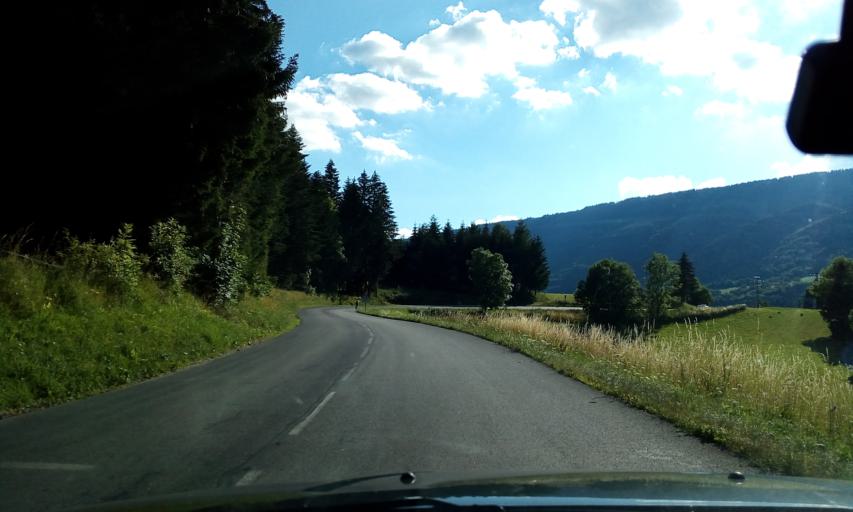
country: FR
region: Rhone-Alpes
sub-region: Departement de l'Isere
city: Lans-en-Vercors
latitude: 45.1609
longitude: 5.6207
